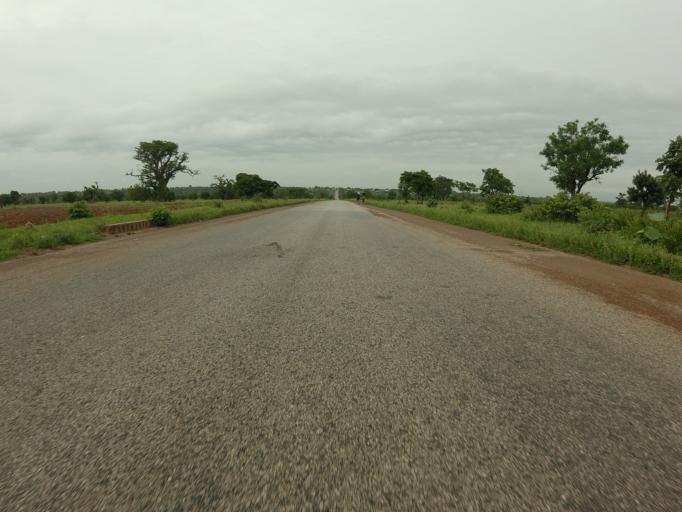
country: GH
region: Northern
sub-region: Yendi
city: Yendi
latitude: 9.5000
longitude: -0.0246
